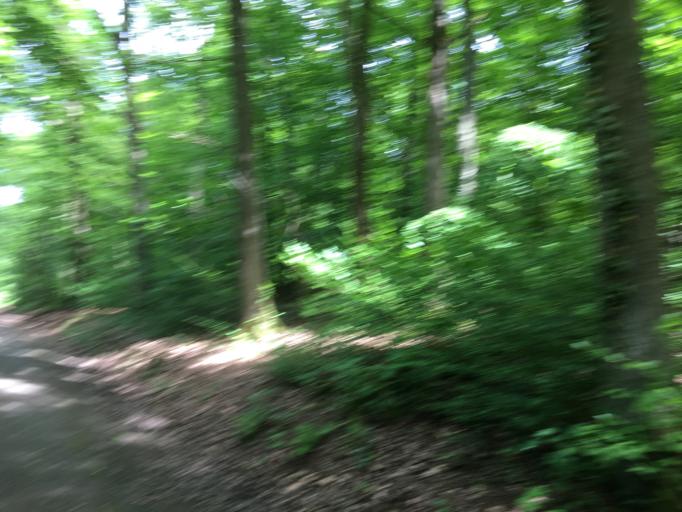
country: DE
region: Rheinland-Pfalz
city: Trier
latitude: 49.7522
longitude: 6.6591
